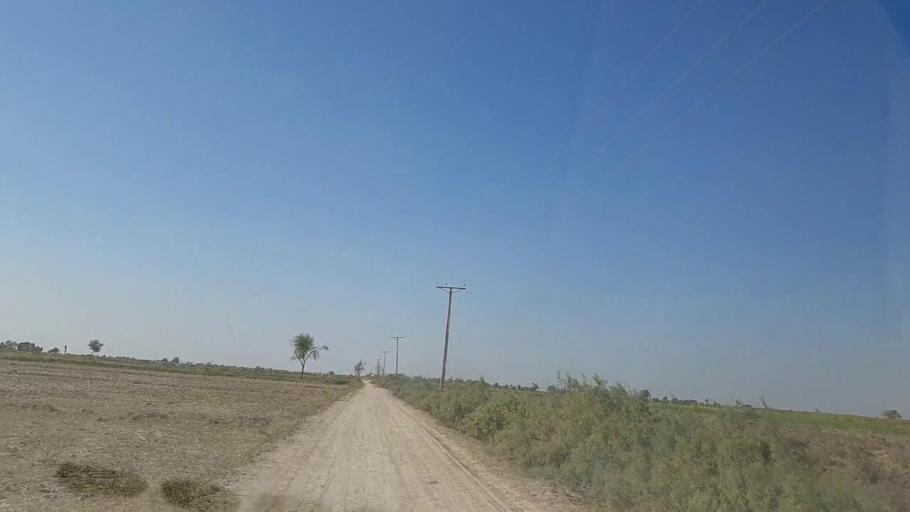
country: PK
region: Sindh
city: Digri
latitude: 25.1263
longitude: 69.0649
